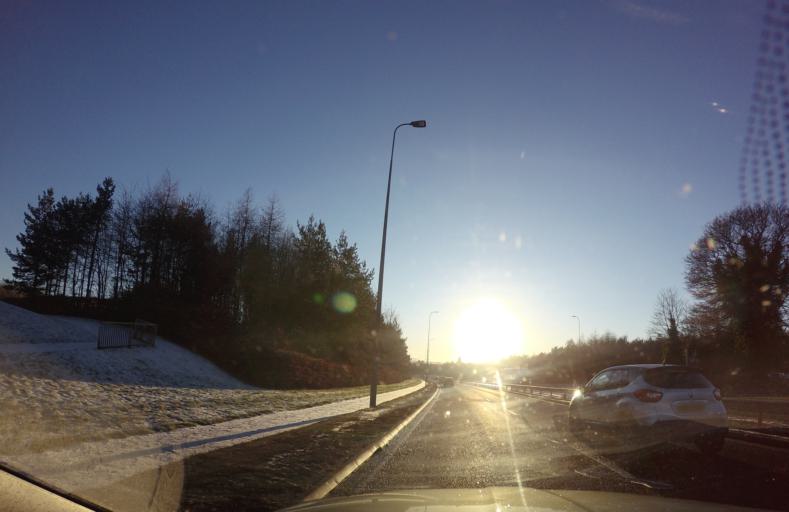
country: GB
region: Scotland
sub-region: Angus
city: Muirhead
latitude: 56.4700
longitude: -3.0586
